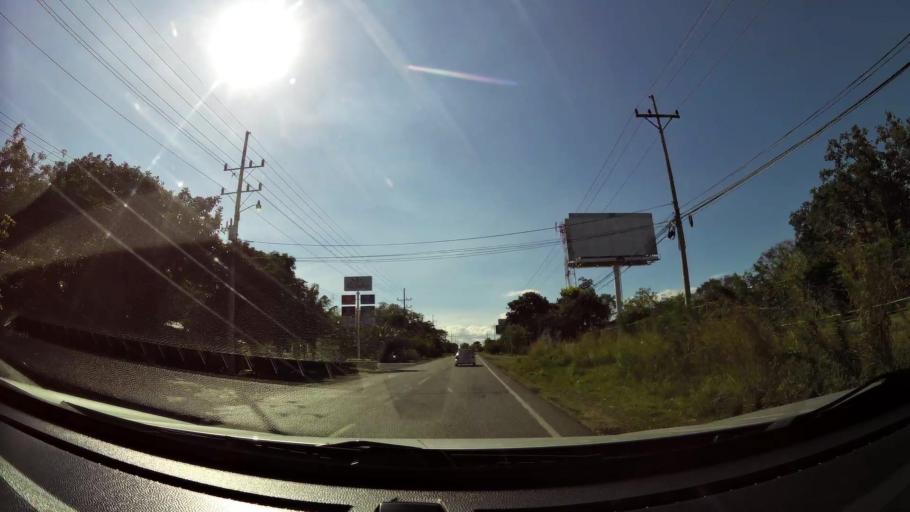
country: CR
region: Guanacaste
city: Liberia
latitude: 10.6134
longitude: -85.4878
